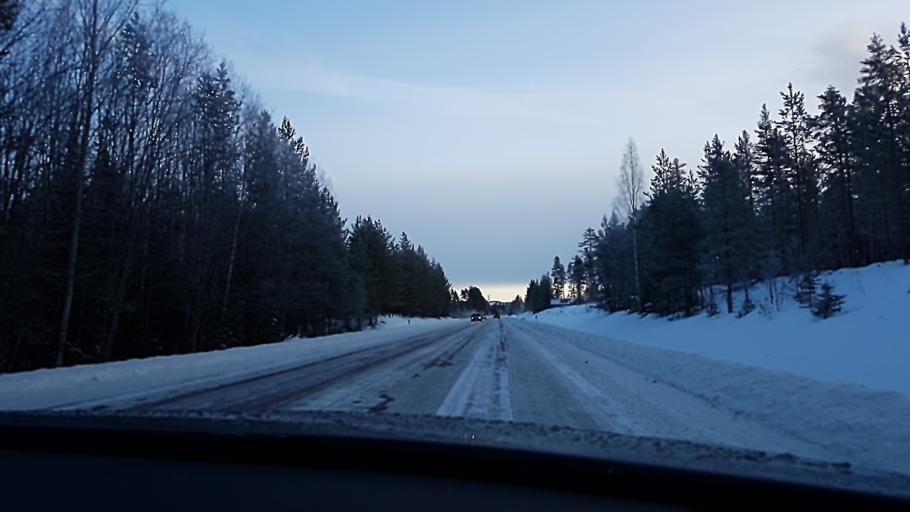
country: SE
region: Jaemtland
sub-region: Bergs Kommun
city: Hoverberg
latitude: 62.4942
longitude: 14.4703
